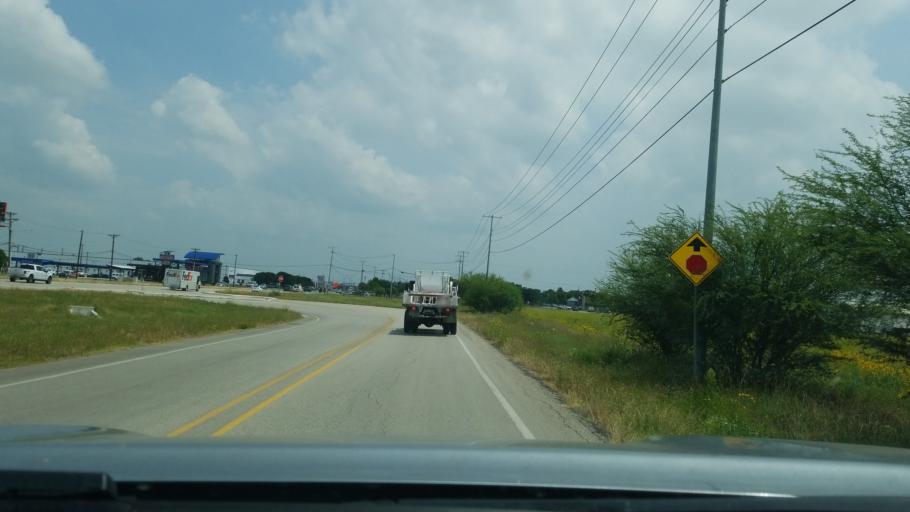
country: US
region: Texas
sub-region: Comal County
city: New Braunfels
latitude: 29.7350
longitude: -98.0860
